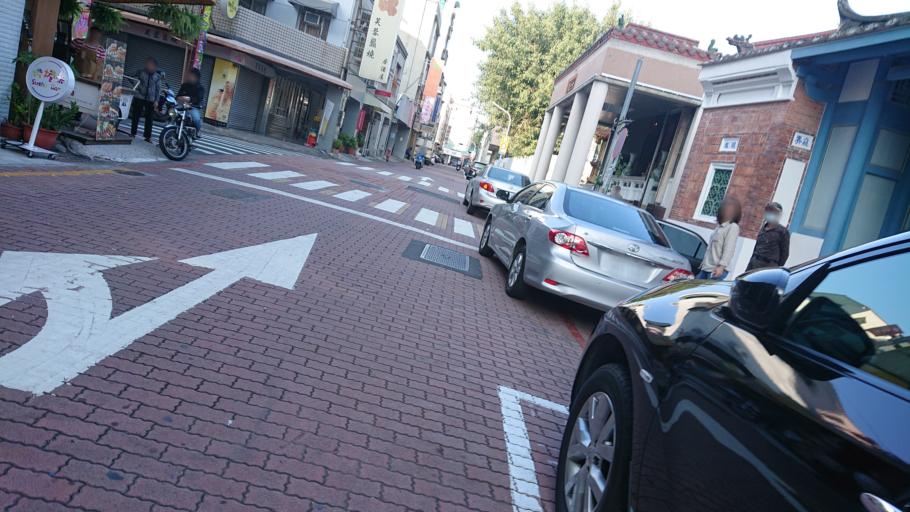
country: TW
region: Taiwan
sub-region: Tainan
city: Tainan
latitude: 22.9978
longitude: 120.2023
